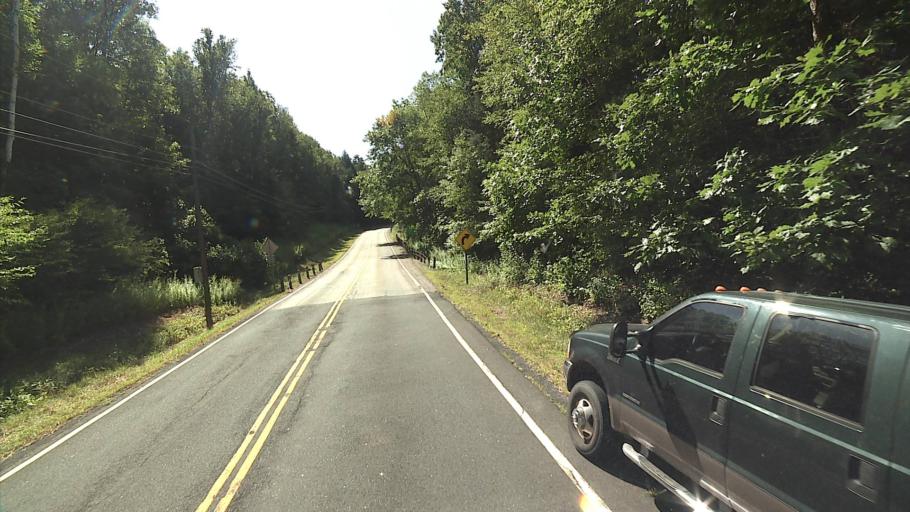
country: US
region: Connecticut
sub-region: Litchfield County
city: Plymouth
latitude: 41.7086
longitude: -73.0556
